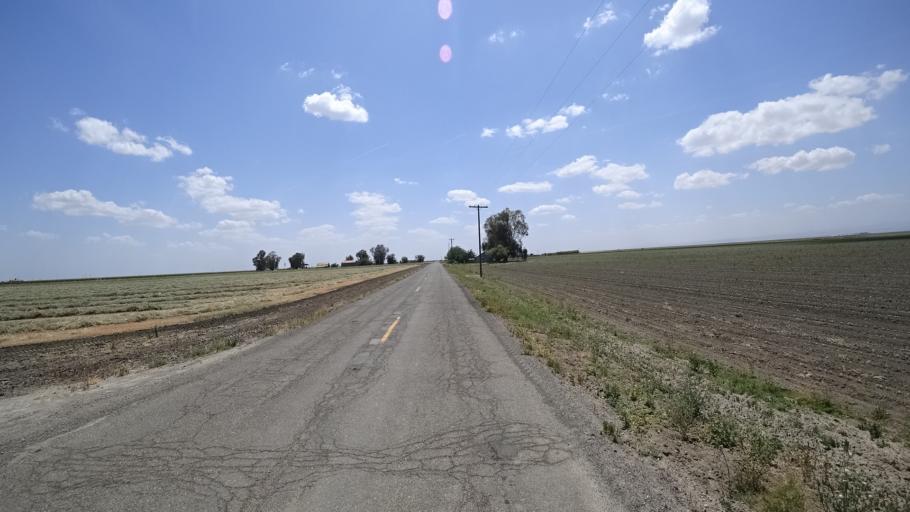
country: US
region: California
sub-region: Kings County
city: Stratford
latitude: 36.1593
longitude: -119.8160
